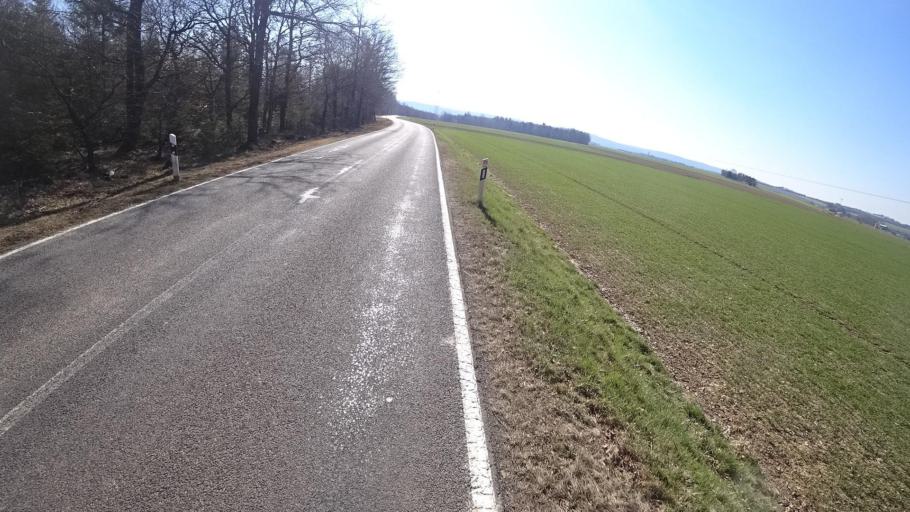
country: DE
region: Rheinland-Pfalz
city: Mutterschied
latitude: 49.9886
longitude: 7.5770
